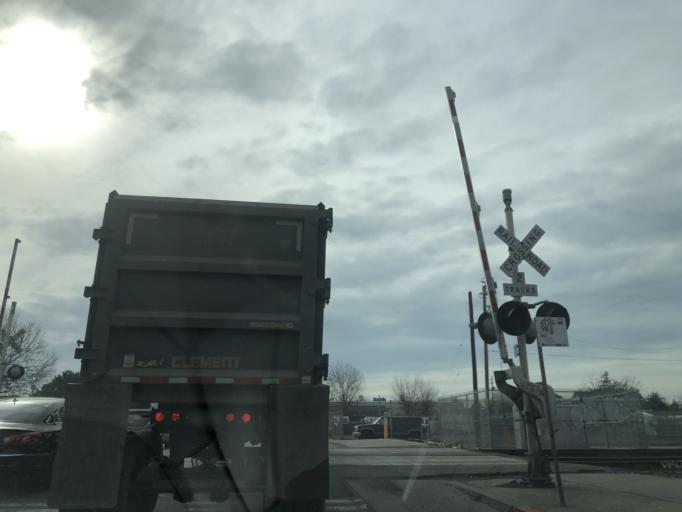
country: US
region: California
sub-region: Alameda County
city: San Leandro
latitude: 37.7380
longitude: -122.1814
